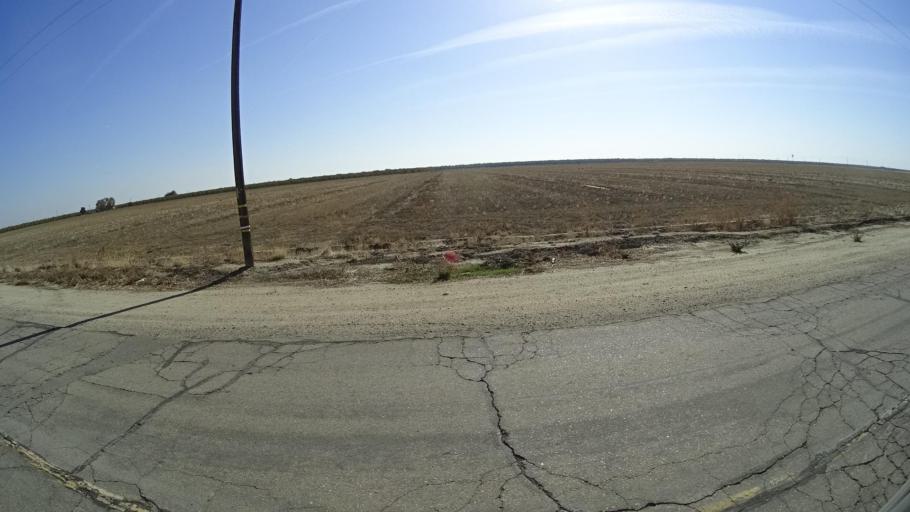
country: US
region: California
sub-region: Kern County
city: Wasco
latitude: 35.6670
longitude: -119.3797
